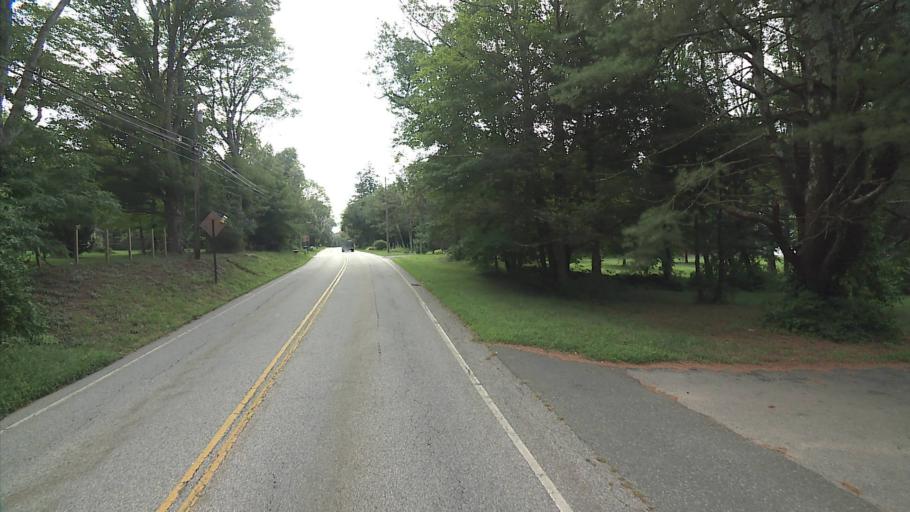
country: US
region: Connecticut
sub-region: Middlesex County
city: East Haddam
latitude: 41.4405
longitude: -72.4172
